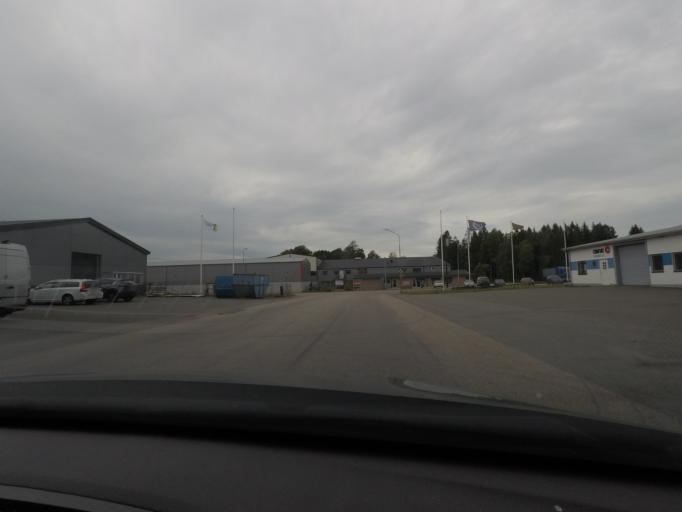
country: SE
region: Skane
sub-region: Osby Kommun
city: Osby
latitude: 56.3839
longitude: 13.9734
